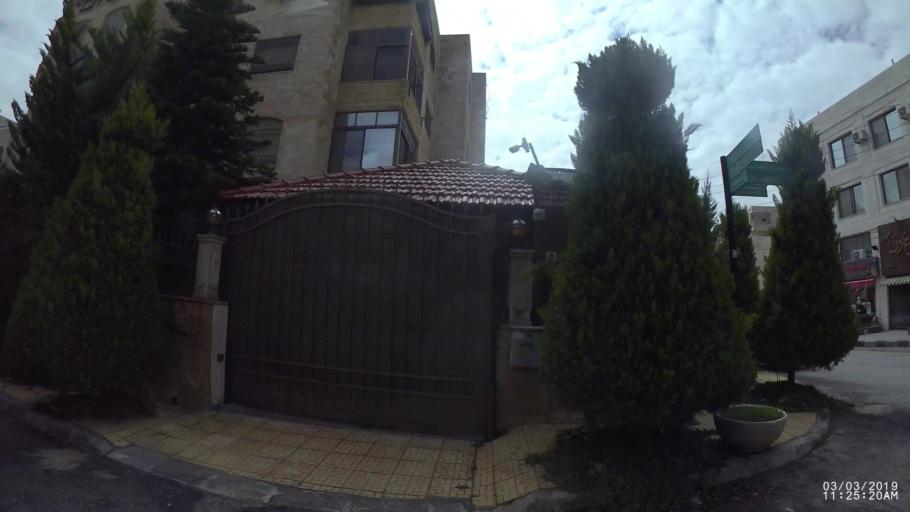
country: JO
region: Amman
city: Amman
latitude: 31.9997
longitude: 35.9164
